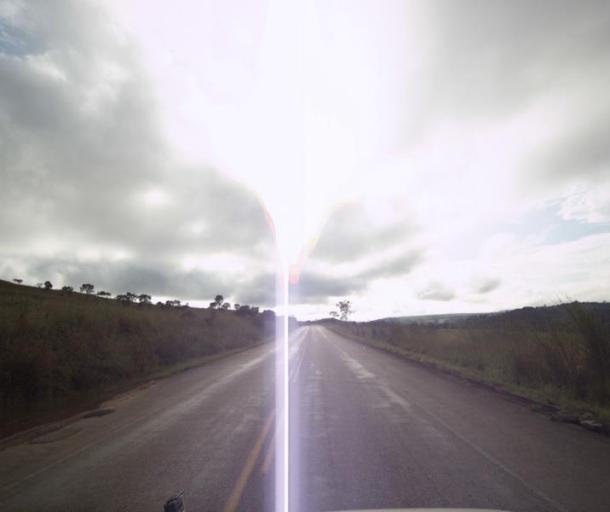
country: BR
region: Goias
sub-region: Pirenopolis
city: Pirenopolis
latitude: -15.7320
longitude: -48.7117
